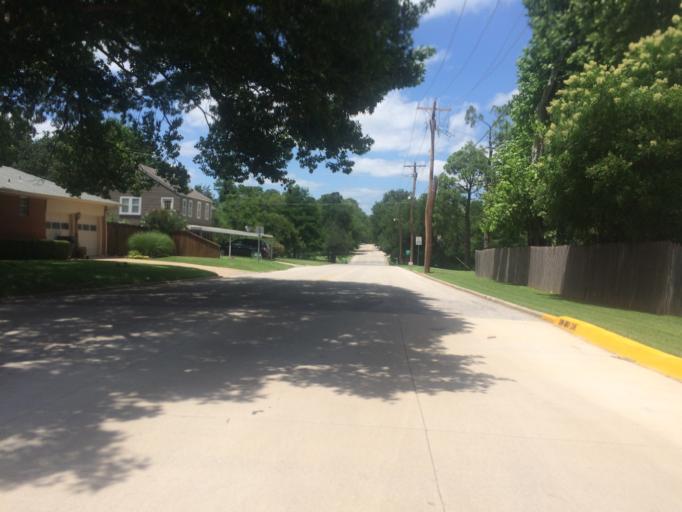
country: US
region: Oklahoma
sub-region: Cleveland County
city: Norman
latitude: 35.2112
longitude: -97.4324
